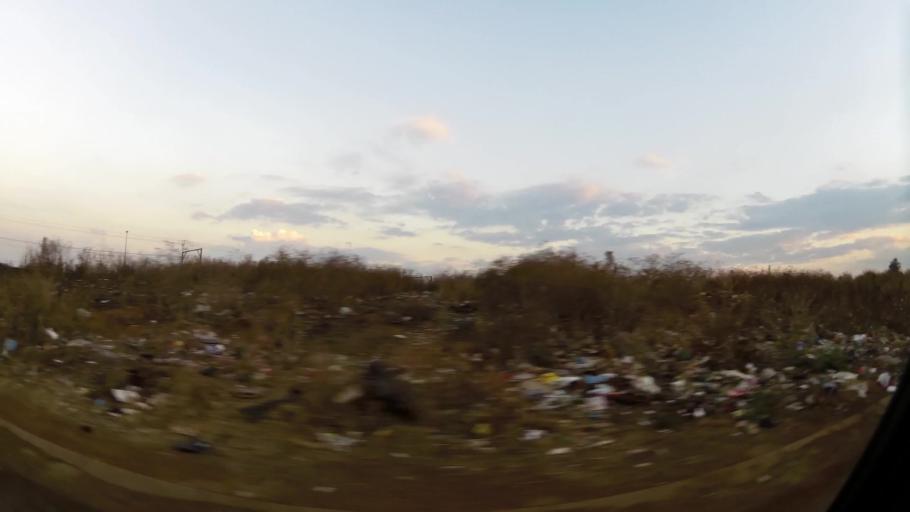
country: ZA
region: Gauteng
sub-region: City of Johannesburg Metropolitan Municipality
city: Orange Farm
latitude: -26.5554
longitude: 27.8791
